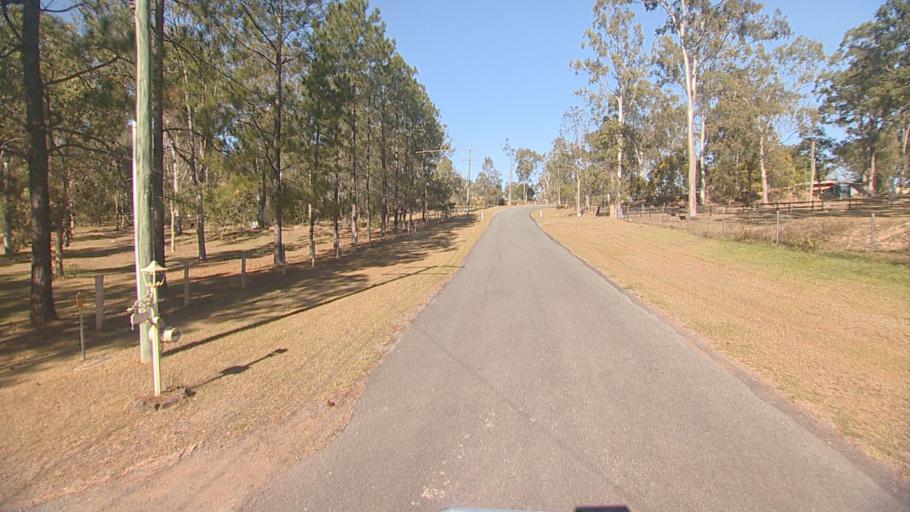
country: AU
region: Queensland
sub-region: Logan
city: Cedar Vale
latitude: -27.8271
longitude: 153.0479
